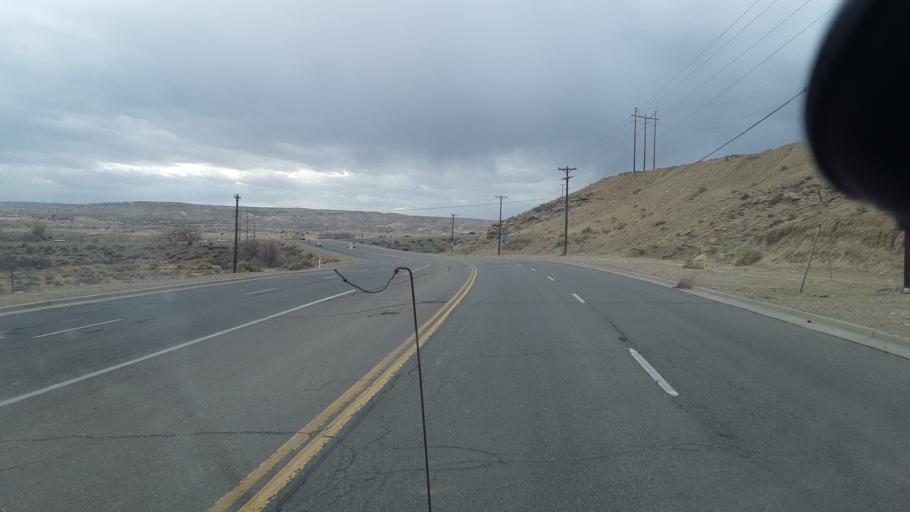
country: US
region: New Mexico
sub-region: San Juan County
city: Farmington
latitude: 36.7413
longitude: -108.2501
